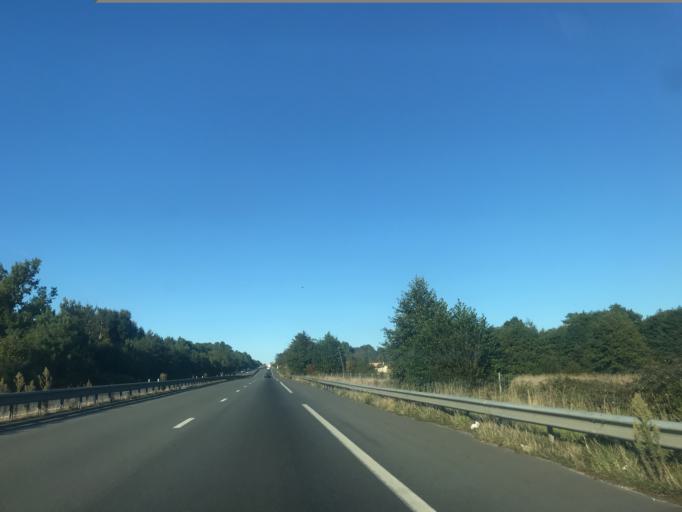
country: FR
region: Poitou-Charentes
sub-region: Departement de la Charente-Maritime
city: Montlieu-la-Garde
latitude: 45.2142
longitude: -0.2930
